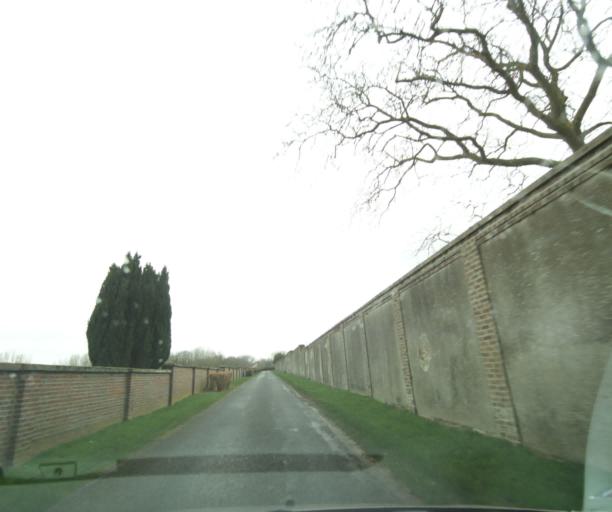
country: FR
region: Picardie
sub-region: Departement de l'Oise
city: Noyon
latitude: 49.5883
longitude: 2.9980
